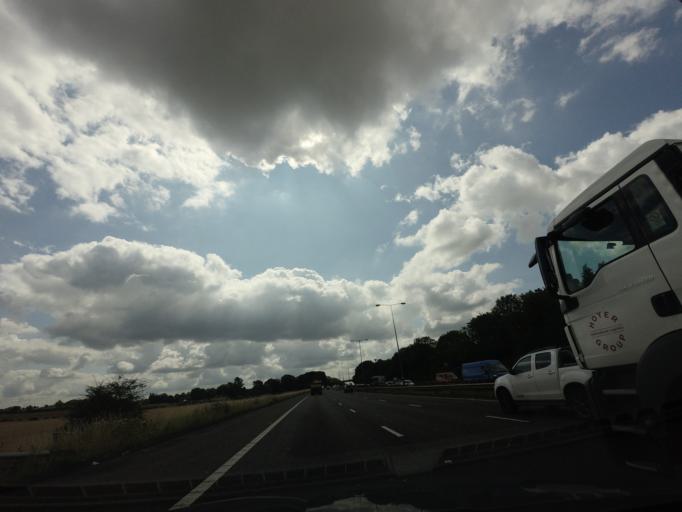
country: GB
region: England
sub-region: Borough of Wigan
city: Shevington
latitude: 53.5428
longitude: -2.6972
